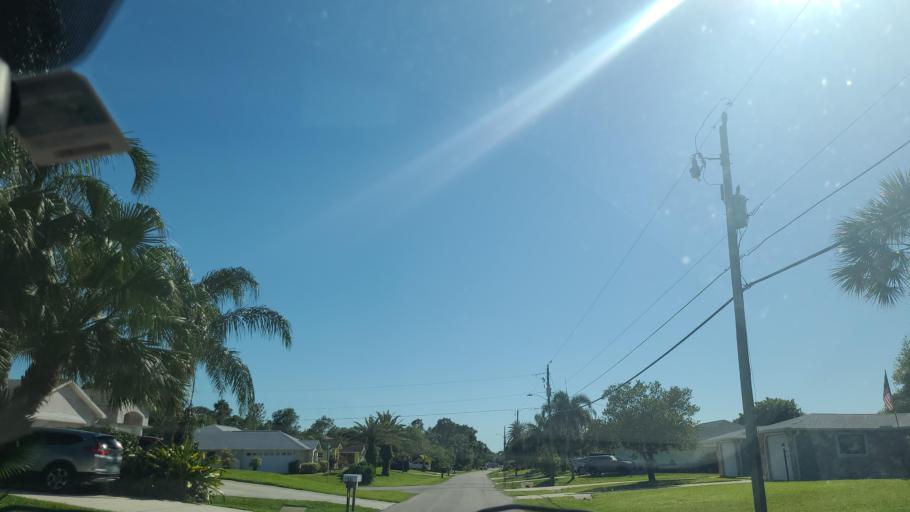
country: US
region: Florida
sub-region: Indian River County
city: Sebastian
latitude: 27.7606
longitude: -80.4814
